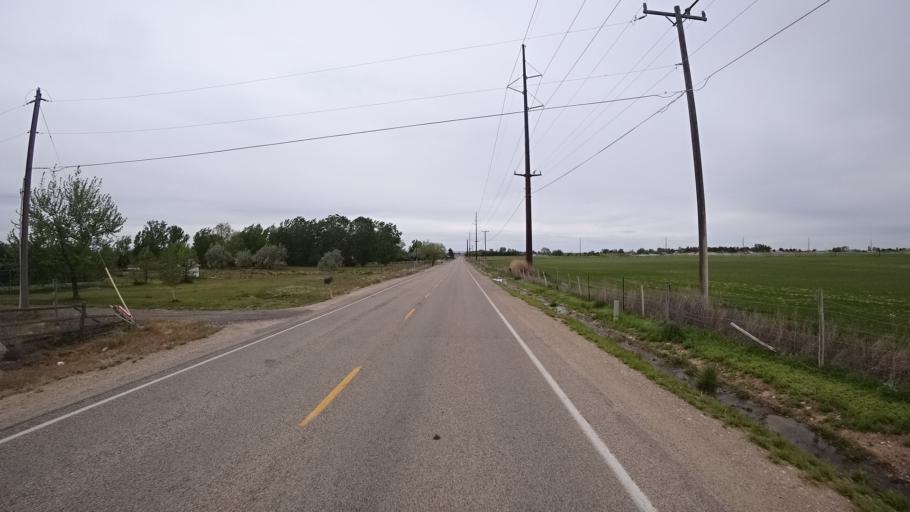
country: US
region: Idaho
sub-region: Ada County
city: Kuna
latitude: 43.4883
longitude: -116.3272
